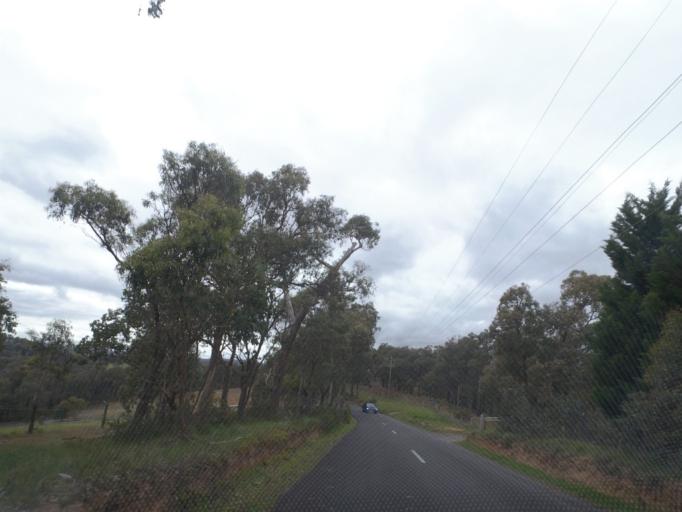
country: AU
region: Victoria
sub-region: Nillumbik
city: Hurstbridge
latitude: -37.6558
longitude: 145.2399
